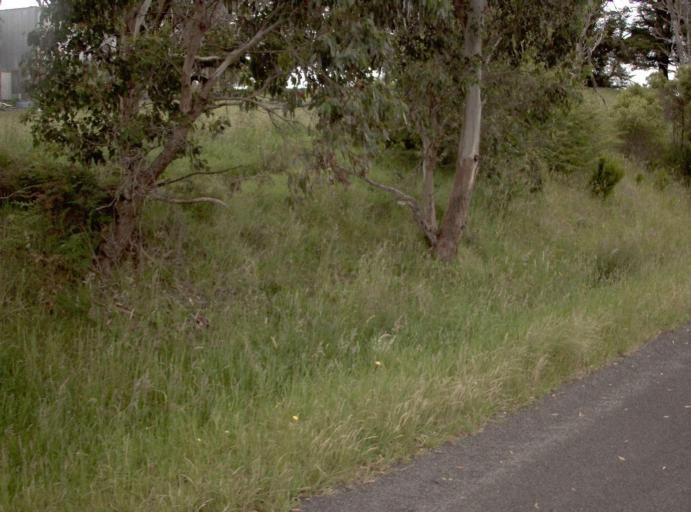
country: AU
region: Victoria
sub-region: Cardinia
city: Koo-Wee-Rup
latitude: -38.3562
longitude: 145.6513
